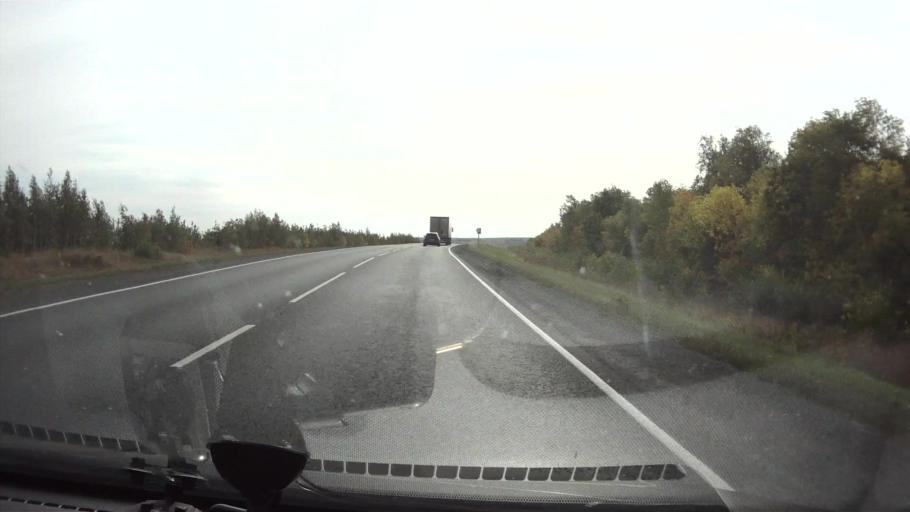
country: RU
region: Saratov
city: Balakovo
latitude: 52.1630
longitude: 47.8238
